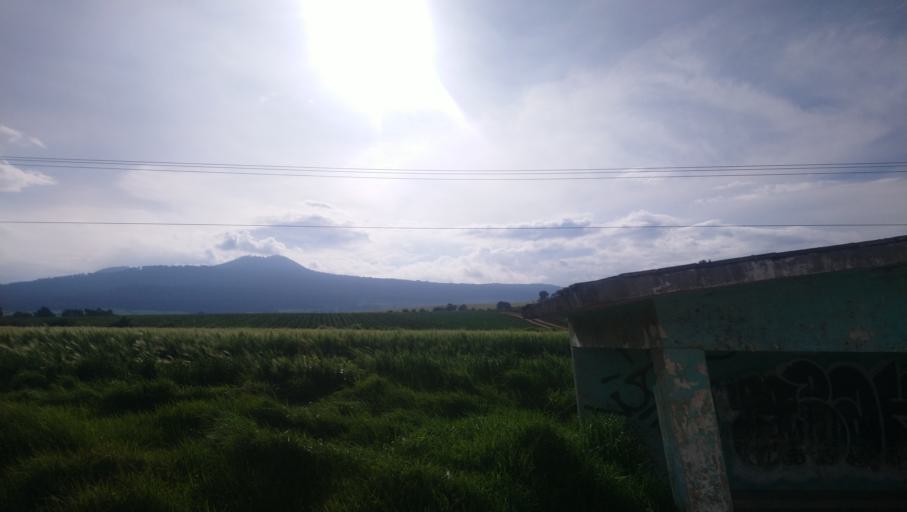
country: MX
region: Mexico
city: Juchitepec de Mariano Riva Palacio
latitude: 19.1169
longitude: -98.9364
